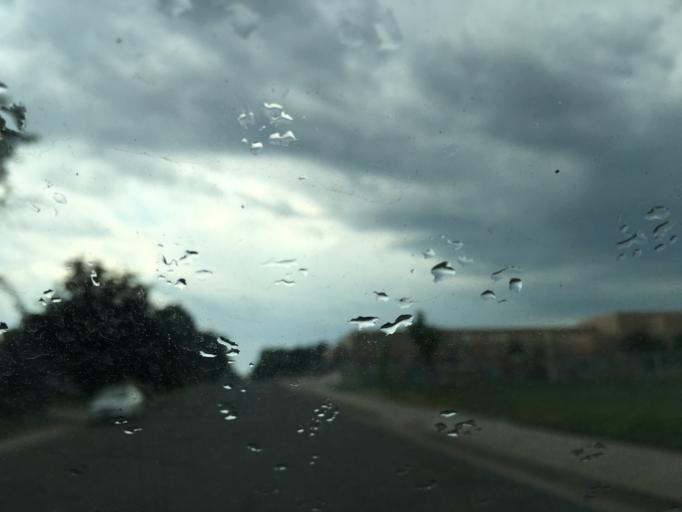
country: US
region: Colorado
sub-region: Arapahoe County
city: Sheridan
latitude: 39.6766
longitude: -105.0388
